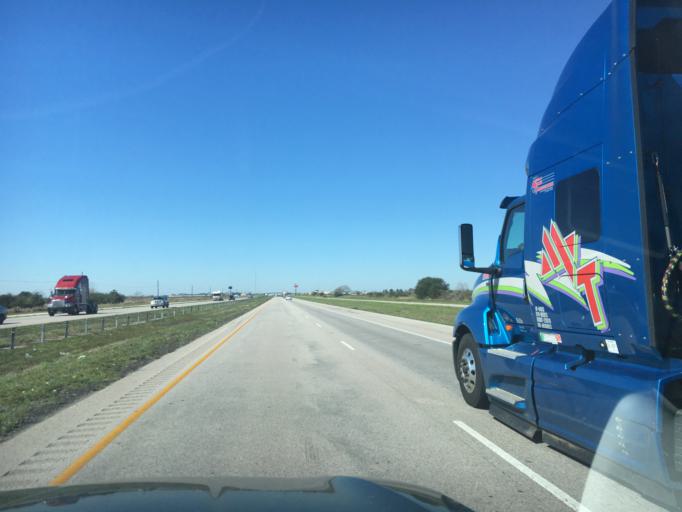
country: US
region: Texas
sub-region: Colorado County
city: Eagle Lake
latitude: 29.7451
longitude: -96.3135
